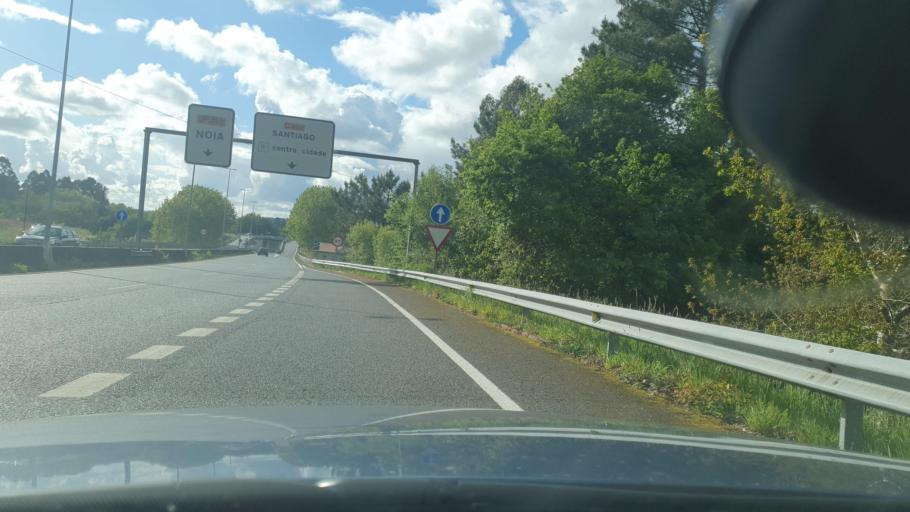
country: ES
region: Galicia
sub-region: Provincia da Coruna
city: Santiago de Compostela
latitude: 42.8679
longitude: -8.5725
